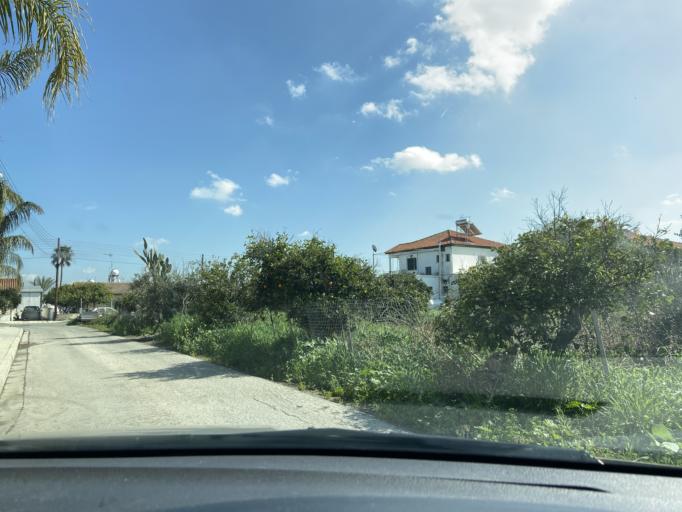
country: CY
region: Lefkosia
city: Dali
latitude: 35.0235
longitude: 33.3915
